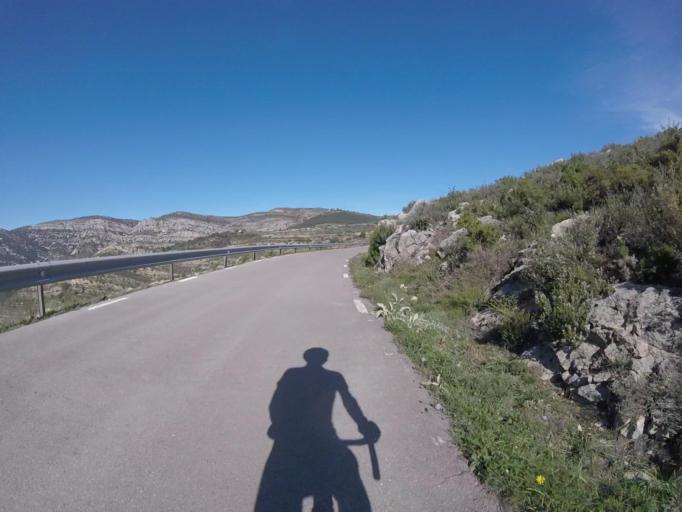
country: ES
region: Valencia
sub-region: Provincia de Castello
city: Sarratella
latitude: 40.2934
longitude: 0.0310
